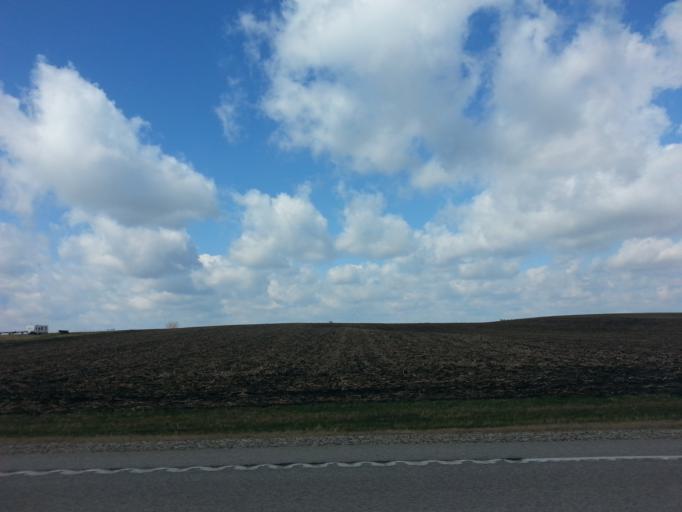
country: US
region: Minnesota
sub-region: Dodge County
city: Mantorville
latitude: 44.0802
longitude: -92.8004
